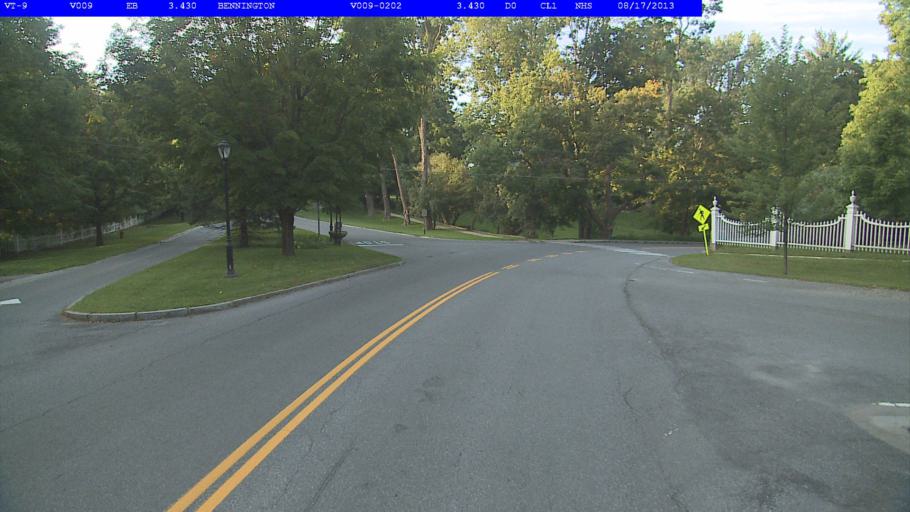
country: US
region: Vermont
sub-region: Bennington County
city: Bennington
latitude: 42.8840
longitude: -73.2134
